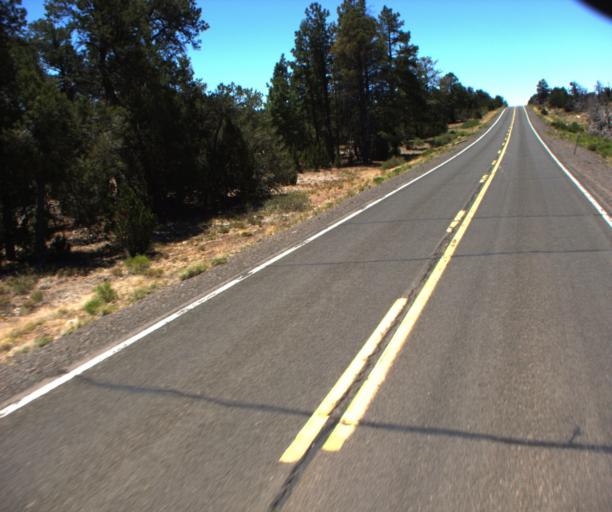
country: US
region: Arizona
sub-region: Coconino County
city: LeChee
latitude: 34.7073
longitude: -111.0985
